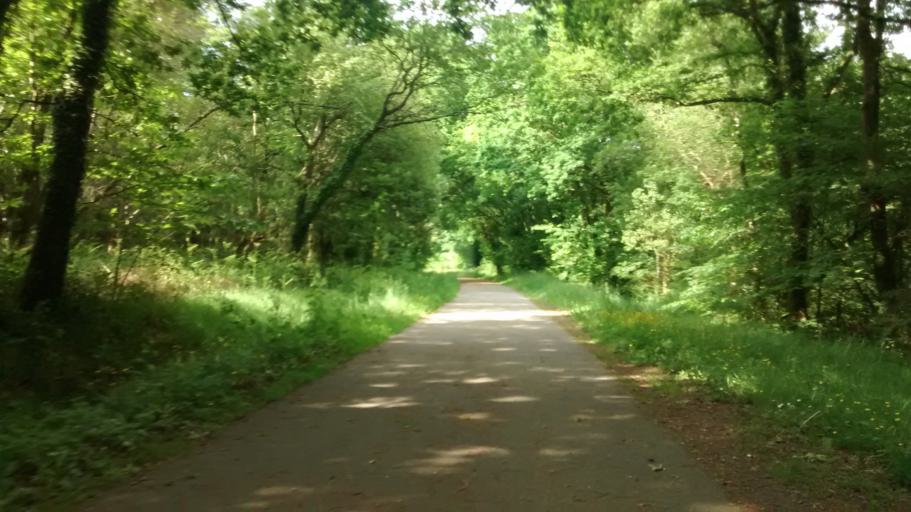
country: FR
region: Brittany
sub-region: Departement du Morbihan
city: Questembert
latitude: 47.6925
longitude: -2.4360
